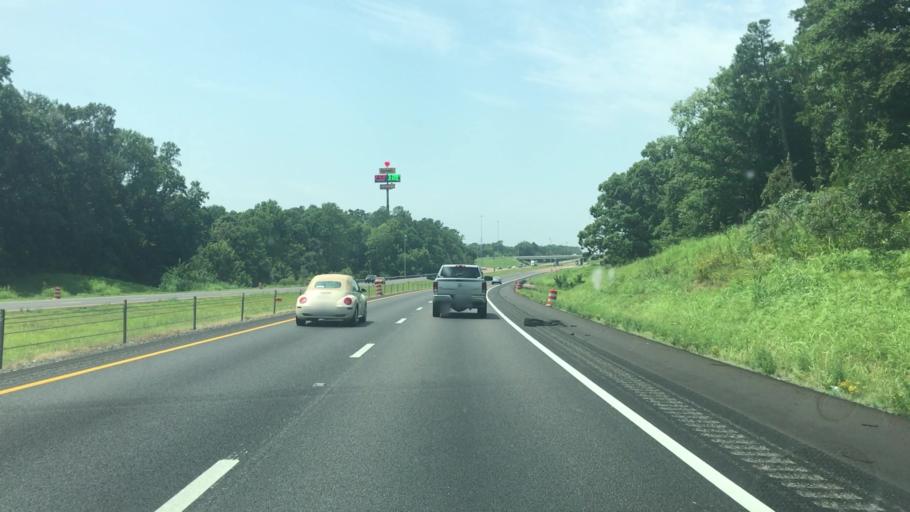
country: US
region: Tennessee
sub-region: Madison County
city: Jackson
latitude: 35.6815
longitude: -88.7350
